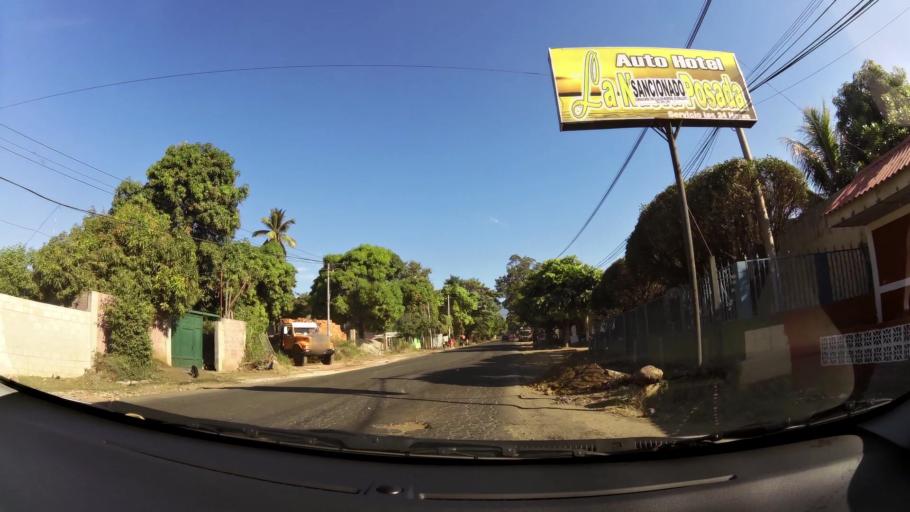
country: SV
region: Sonsonate
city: Sonzacate
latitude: 13.7418
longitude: -89.7090
